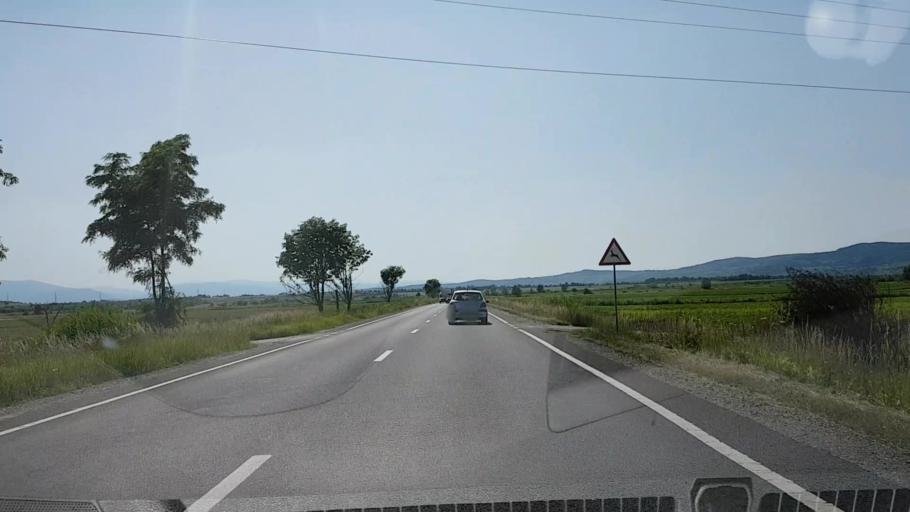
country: RO
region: Sibiu
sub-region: Comuna Porumbacu de Jos
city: Porumbacu de Jos
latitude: 45.7568
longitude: 24.4999
